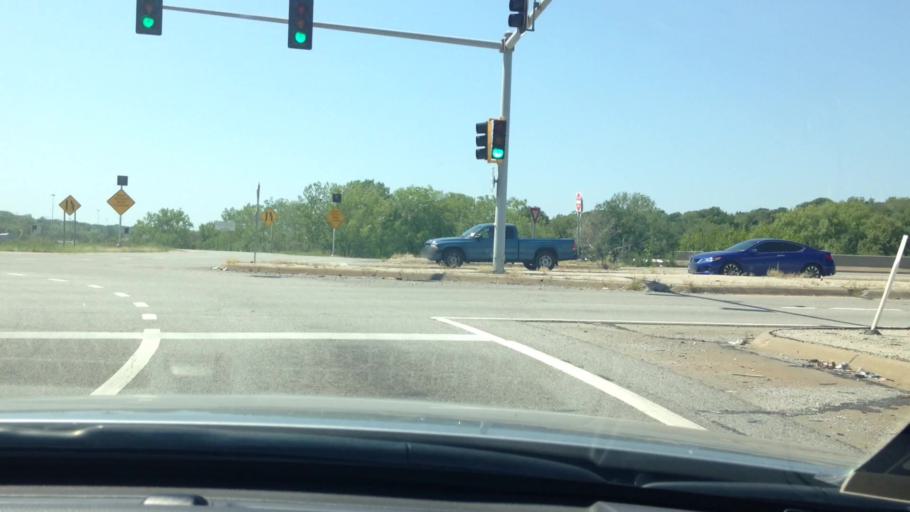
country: US
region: Kansas
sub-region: Johnson County
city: Roeland Park
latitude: 39.0485
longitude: -94.6464
